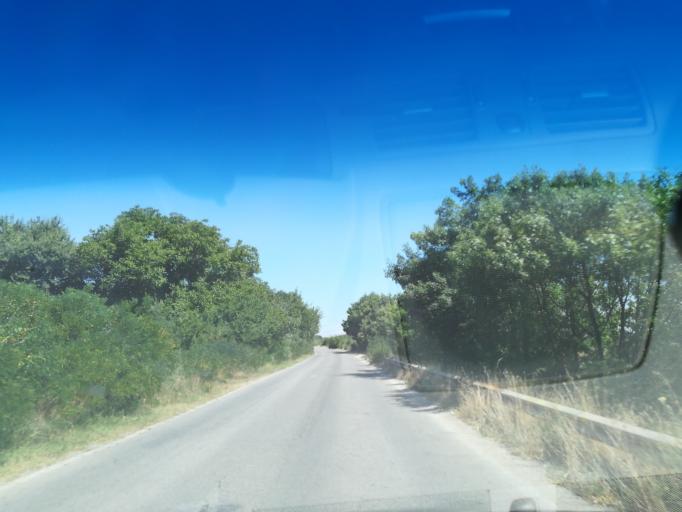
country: BG
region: Plovdiv
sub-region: Obshtina Sadovo
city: Sadovo
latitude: 42.0247
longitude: 24.9934
